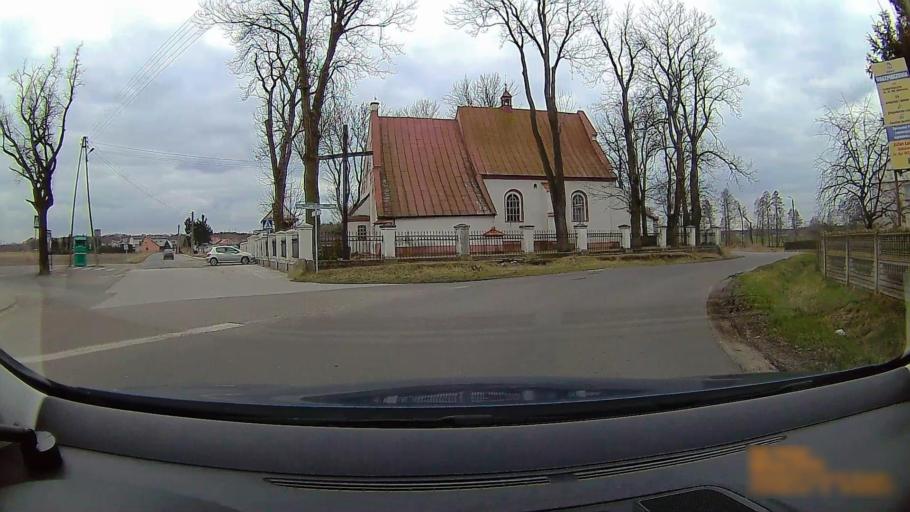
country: PL
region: Greater Poland Voivodeship
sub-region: Powiat koninski
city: Rzgow Pierwszy
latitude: 52.1340
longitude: 18.0571
